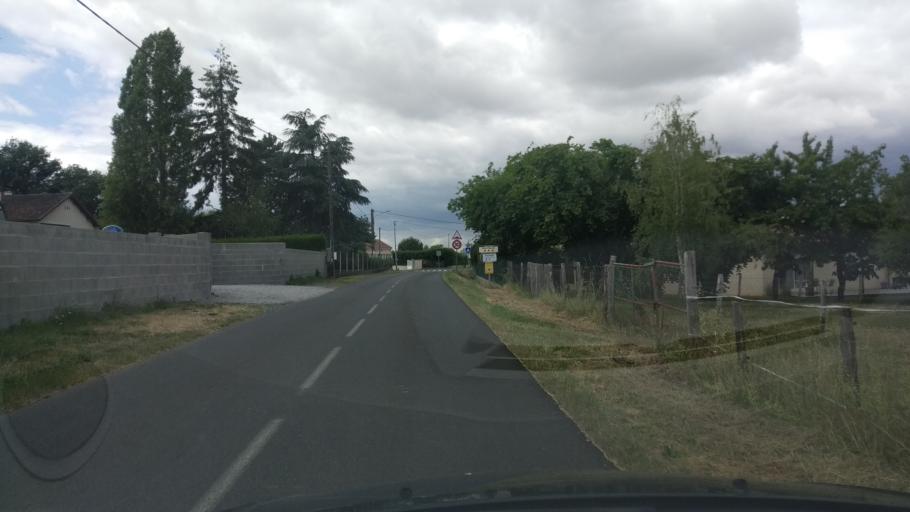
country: FR
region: Poitou-Charentes
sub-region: Departement de la Vienne
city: Vouille
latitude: 46.6282
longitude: 0.1914
